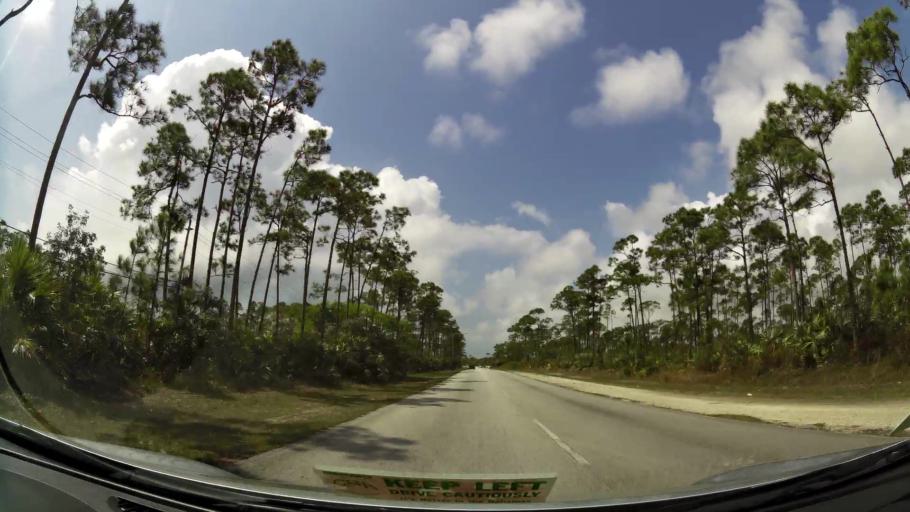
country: BS
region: Freeport
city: Lucaya
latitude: 26.5382
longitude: -78.6333
